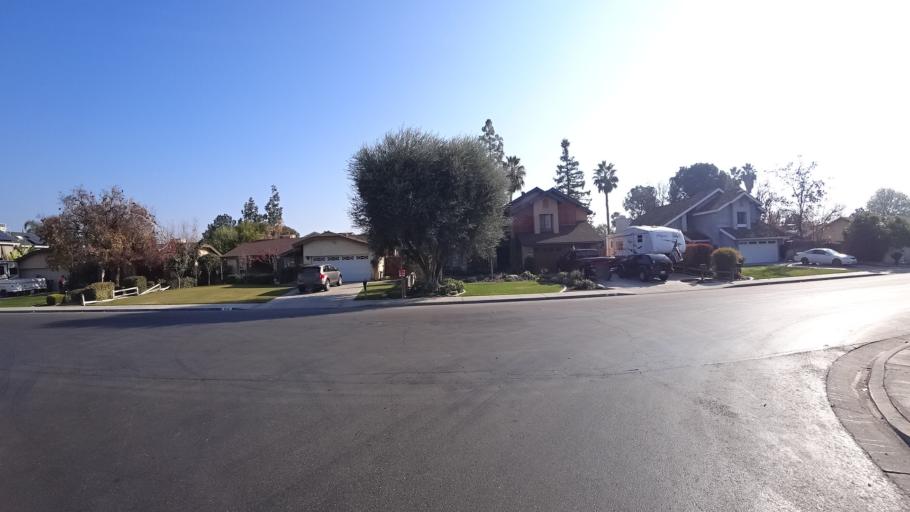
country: US
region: California
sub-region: Kern County
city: Greenacres
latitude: 35.3206
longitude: -119.0885
